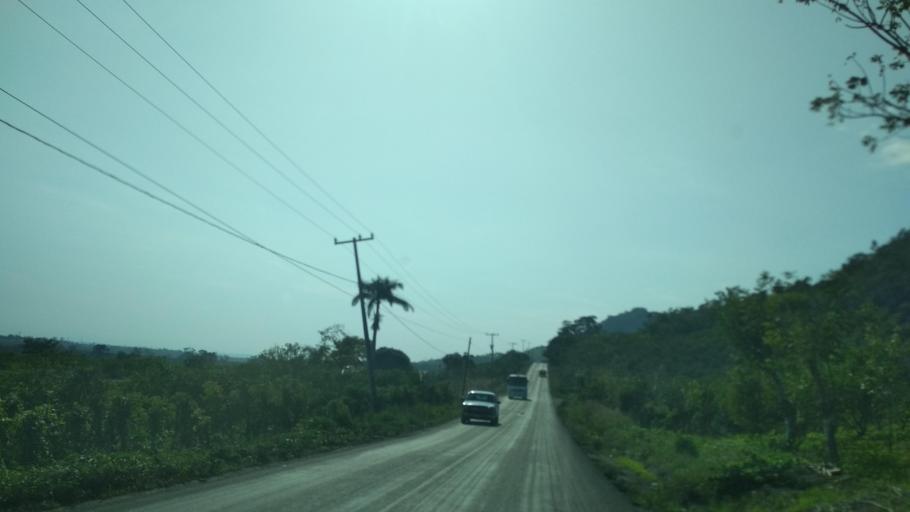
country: MX
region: Veracruz
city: Agua Dulce
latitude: 20.3961
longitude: -97.2700
